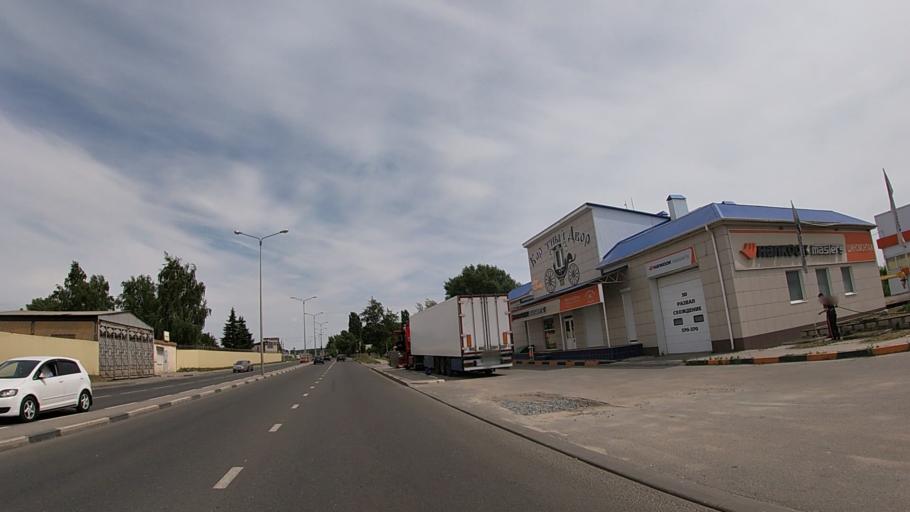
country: RU
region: Belgorod
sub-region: Belgorodskiy Rayon
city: Belgorod
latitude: 50.6162
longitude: 36.5380
